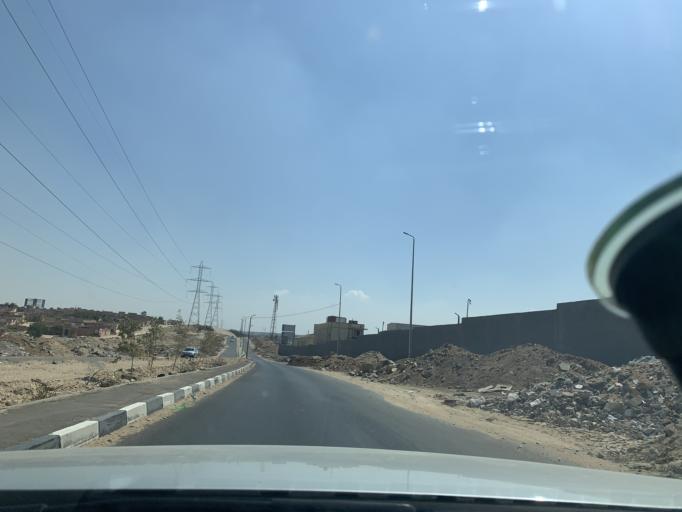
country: EG
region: Muhafazat al Qahirah
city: Cairo
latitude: 30.0277
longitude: 31.3472
